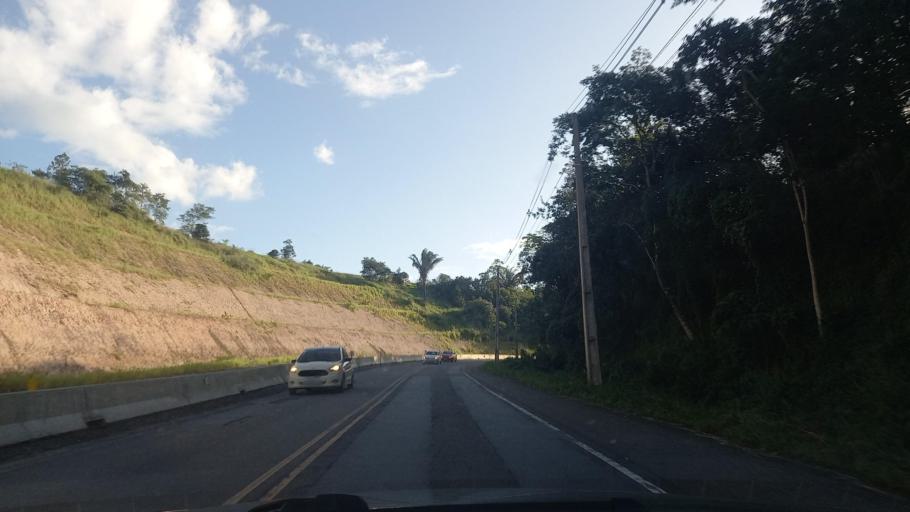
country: BR
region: Alagoas
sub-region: Campo Alegre
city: Campo Alegre
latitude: -9.8218
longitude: -36.2243
